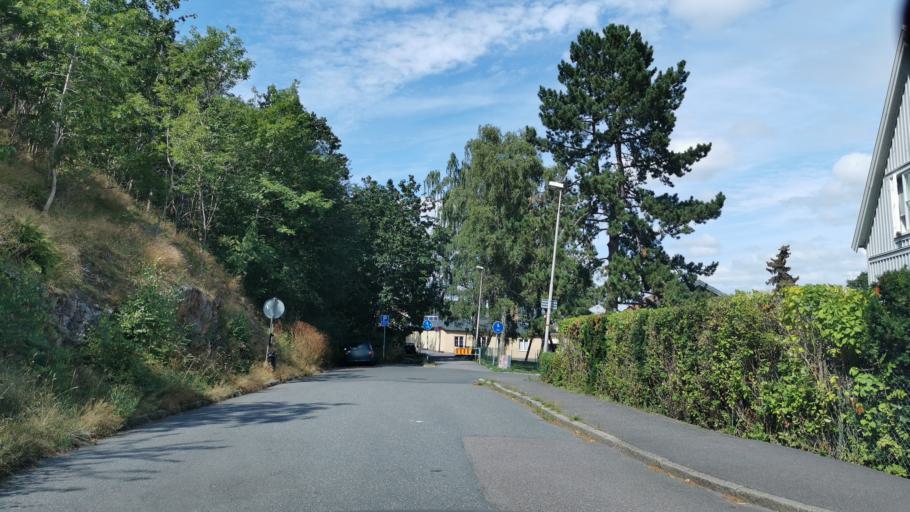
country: SE
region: Vaestra Goetaland
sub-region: Molndal
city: Moelndal
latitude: 57.6727
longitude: 12.0046
